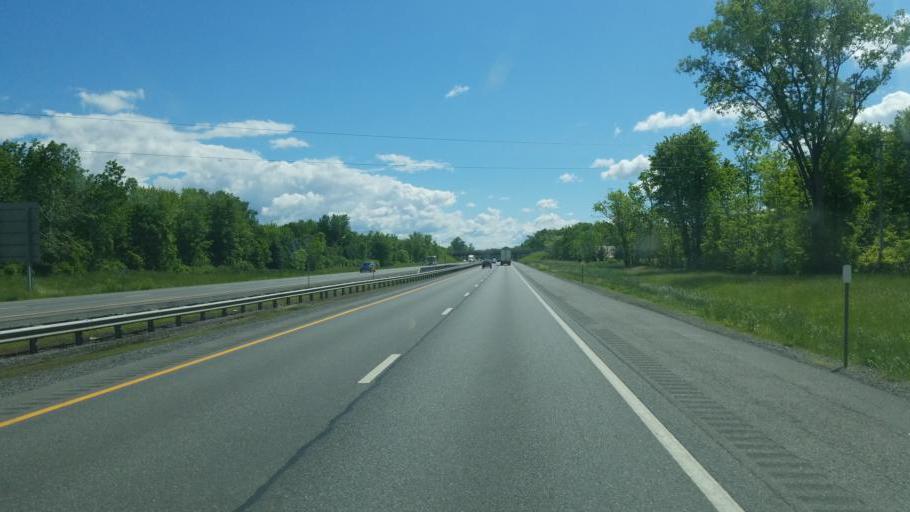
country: US
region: New York
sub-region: Madison County
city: Wampsville
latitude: 43.1061
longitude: -75.6864
